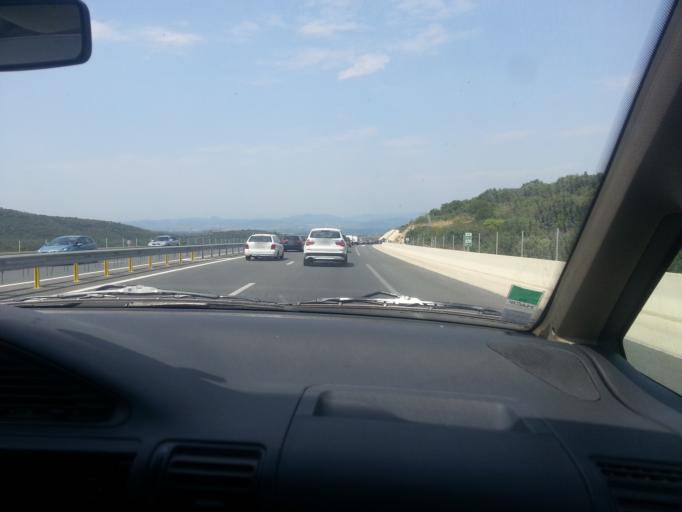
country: FR
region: Languedoc-Roussillon
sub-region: Departement de l'Herault
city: Aniane
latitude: 43.6256
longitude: 3.6137
